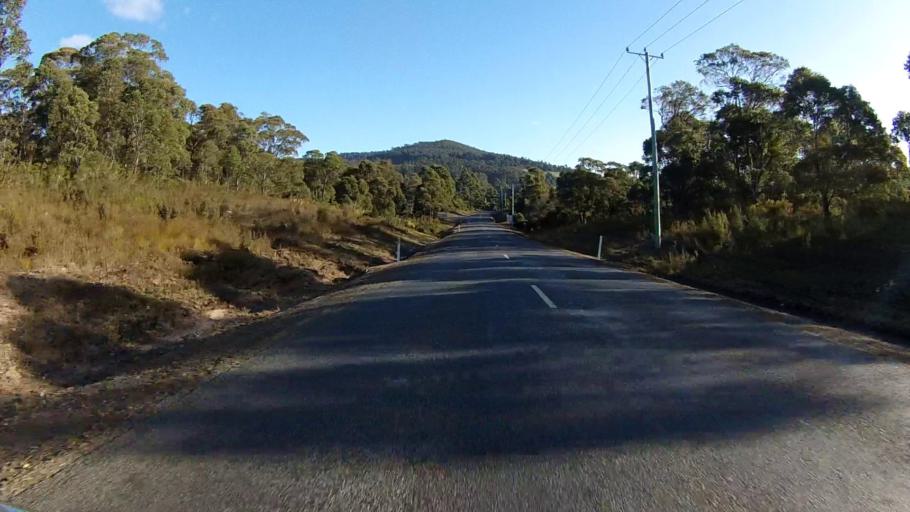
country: AU
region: Tasmania
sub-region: Clarence
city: Sandford
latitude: -43.1424
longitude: 147.8470
